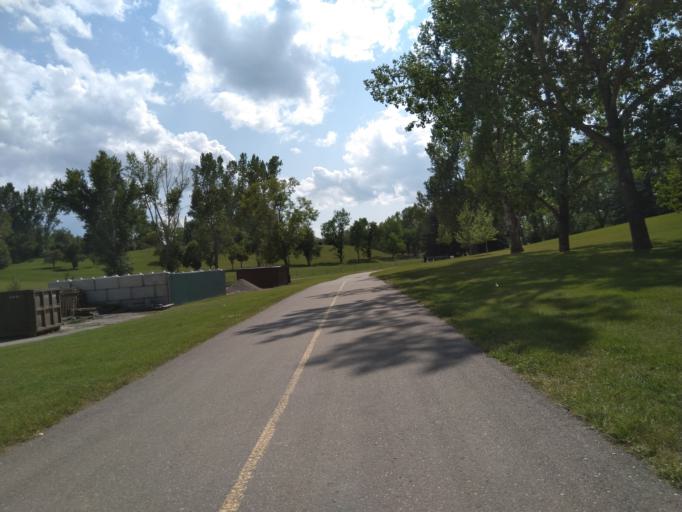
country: CA
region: Alberta
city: Calgary
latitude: 51.0825
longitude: -114.0756
